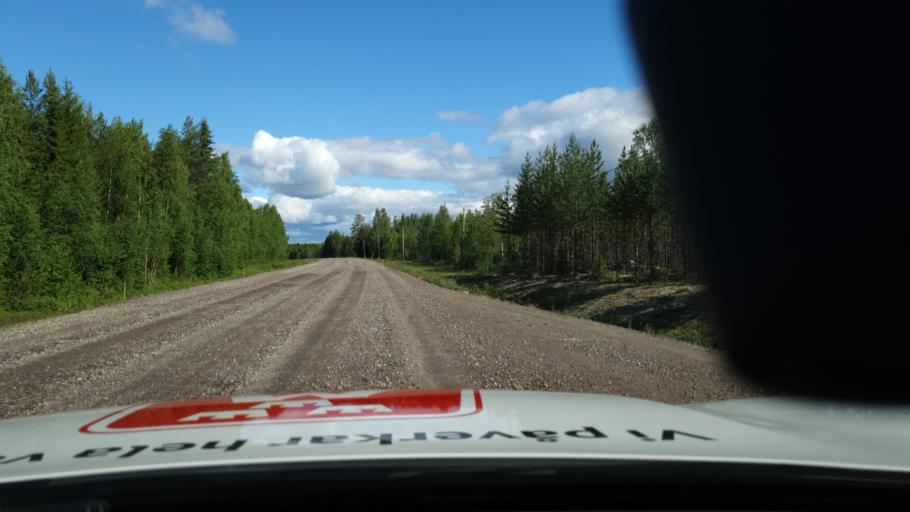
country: SE
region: Norrbotten
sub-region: Alvsbyns Kommun
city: AElvsbyn
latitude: 66.1955
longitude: 20.8857
